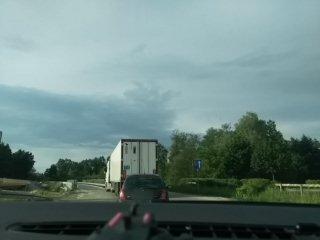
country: PL
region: Subcarpathian Voivodeship
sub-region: Powiat nizanski
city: Jarocin
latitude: 50.6205
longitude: 22.2867
